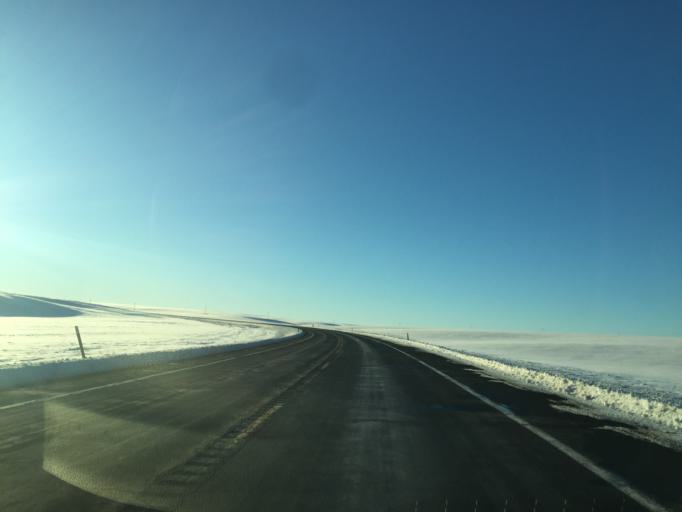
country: US
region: Washington
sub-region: Grant County
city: Soap Lake
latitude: 47.6068
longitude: -119.5025
